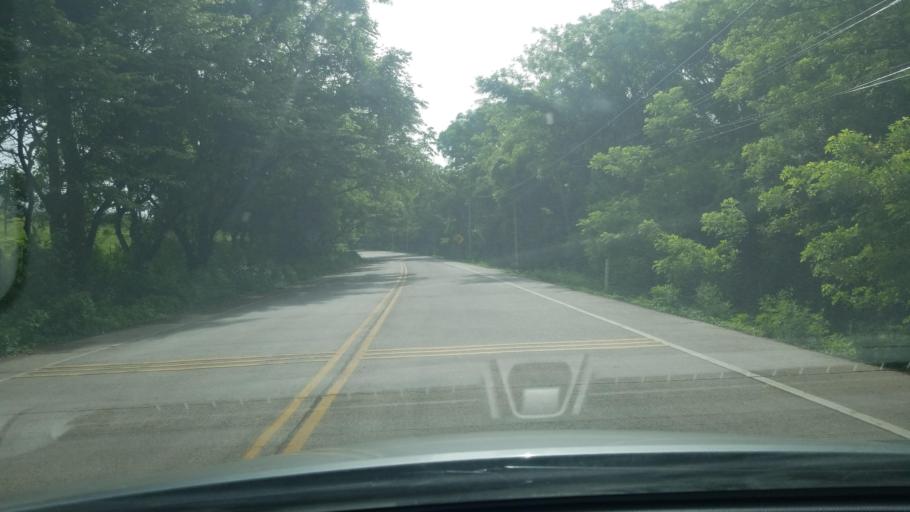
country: HN
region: Copan
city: Copan
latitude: 14.8404
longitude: -89.1454
